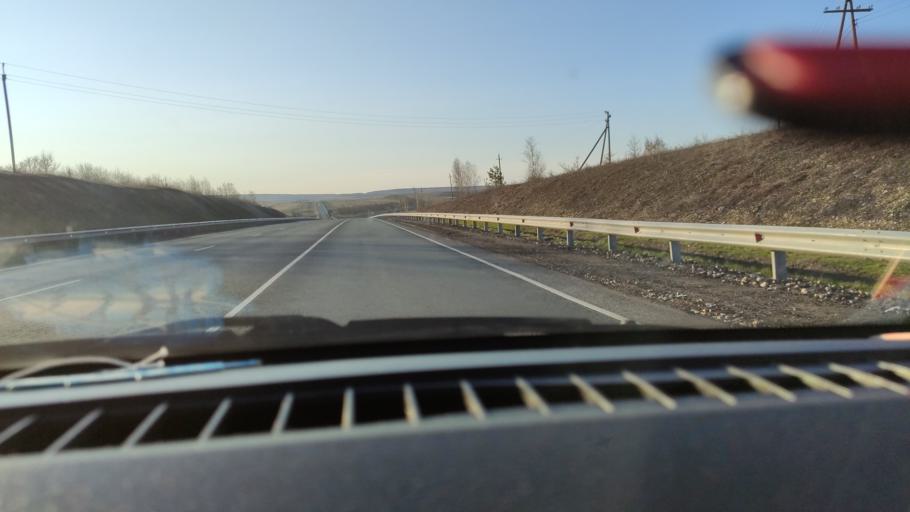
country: RU
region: Saratov
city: Shikhany
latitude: 52.1431
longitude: 47.2034
